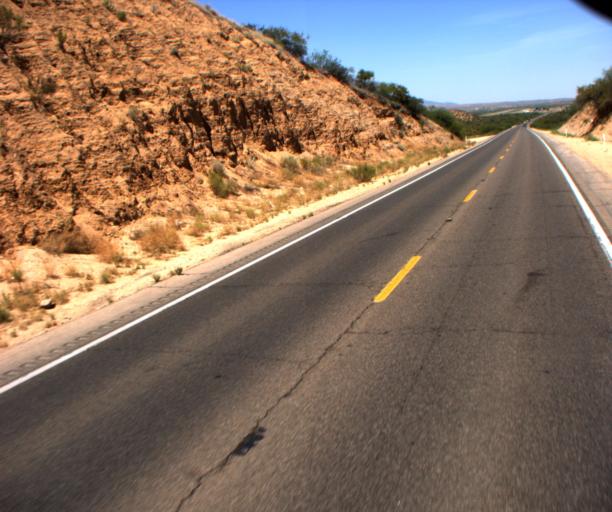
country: US
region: Arizona
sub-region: Gila County
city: Globe
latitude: 33.3494
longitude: -110.6351
